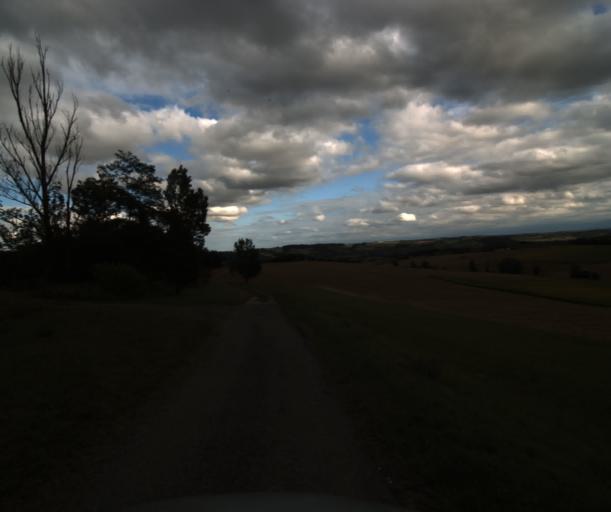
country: FR
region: Midi-Pyrenees
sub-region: Departement de la Haute-Garonne
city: Eaunes
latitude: 43.3983
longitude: 1.3307
